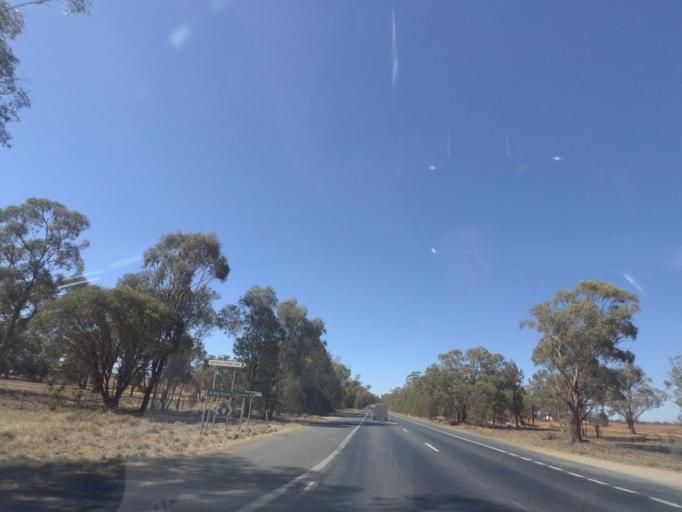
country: AU
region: New South Wales
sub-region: Bland
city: West Wyalong
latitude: -34.2003
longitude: 147.1104
